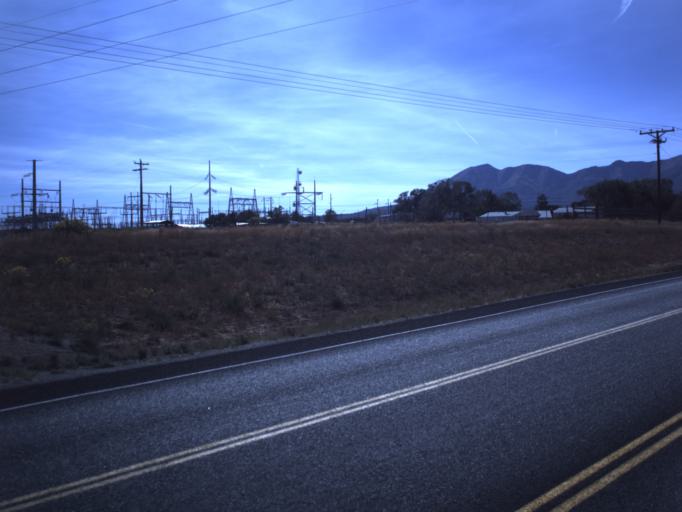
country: US
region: Utah
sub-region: San Juan County
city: Monticello
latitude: 37.8728
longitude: -109.3119
